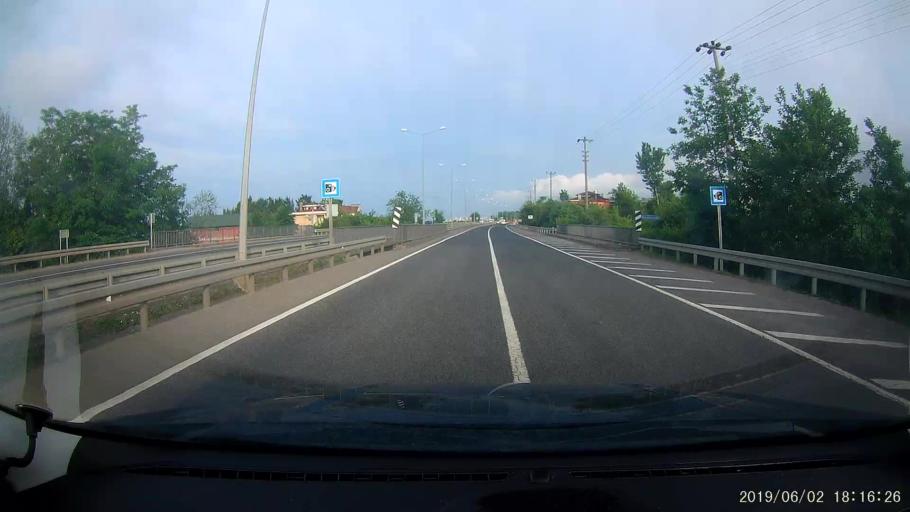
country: TR
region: Ordu
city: Unieh
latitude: 41.1005
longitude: 37.3985
